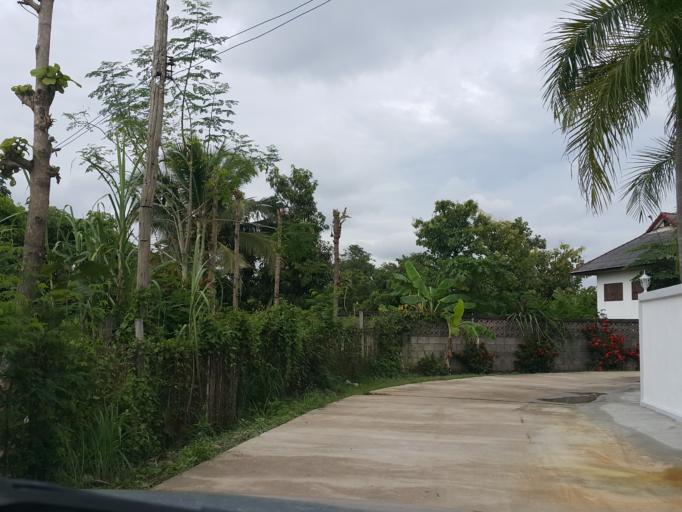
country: TH
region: Chiang Mai
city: San Sai
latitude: 18.8424
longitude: 99.1350
